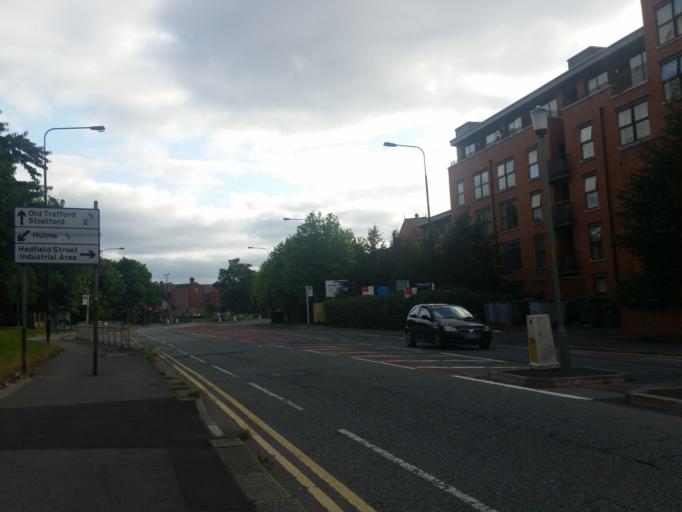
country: GB
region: England
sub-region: Manchester
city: Hulme
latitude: 53.4672
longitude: -2.2664
